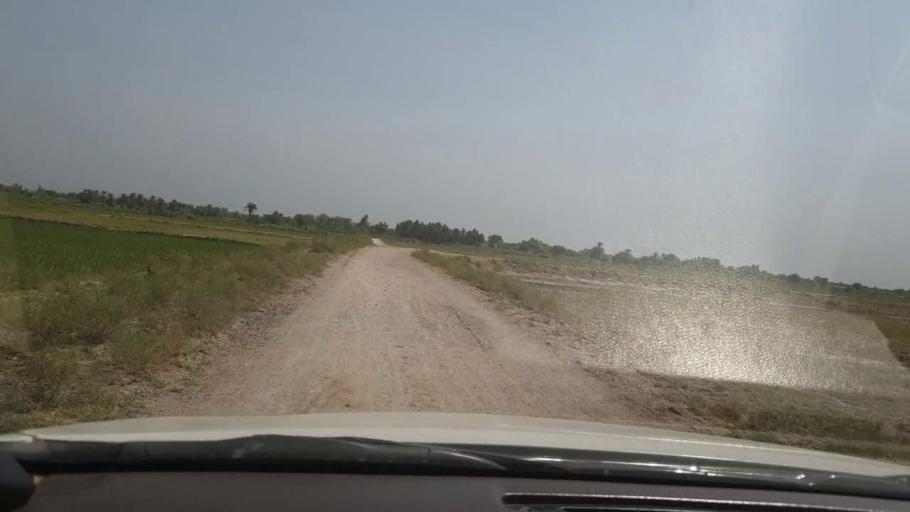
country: PK
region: Sindh
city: Shikarpur
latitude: 27.9224
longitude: 68.6059
